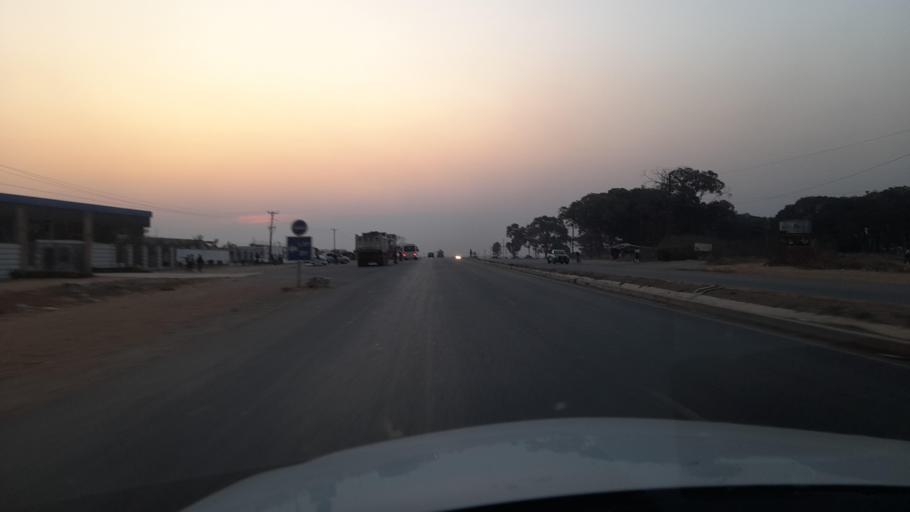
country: ZM
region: Copperbelt
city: Kitwe
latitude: -12.7696
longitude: 28.1811
